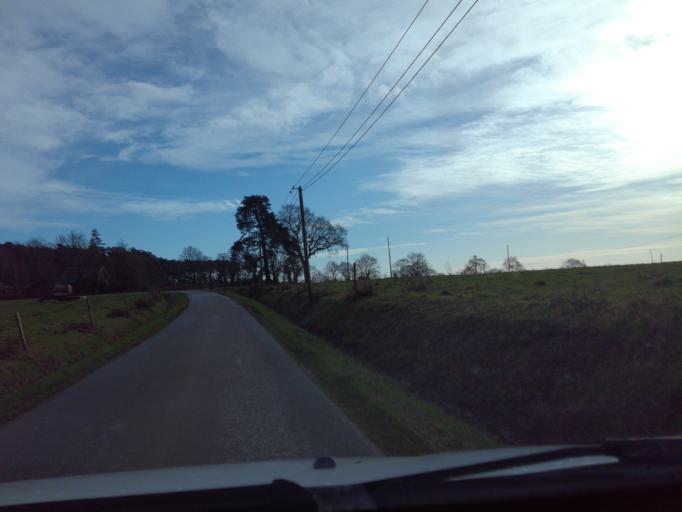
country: FR
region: Brittany
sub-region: Departement d'Ille-et-Vilaine
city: Liffre
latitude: 48.1999
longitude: -1.4916
